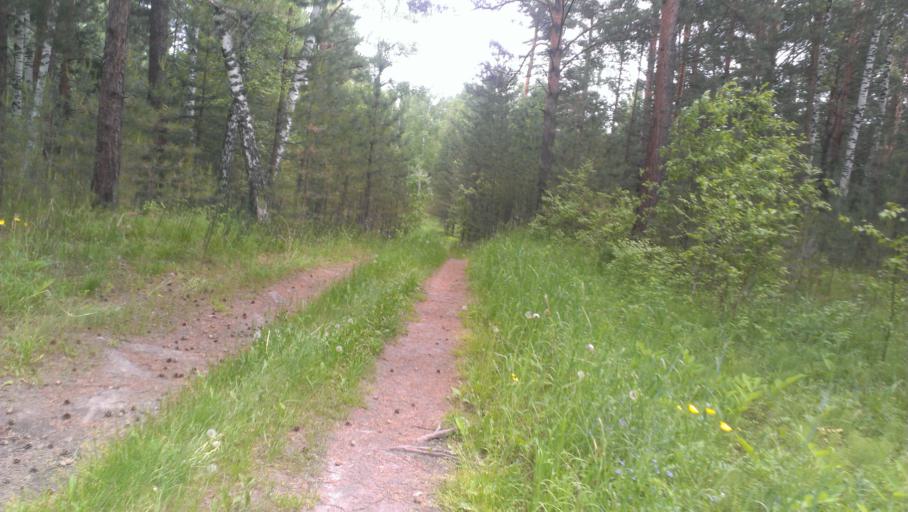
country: RU
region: Altai Krai
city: Sannikovo
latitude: 53.3488
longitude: 84.0384
